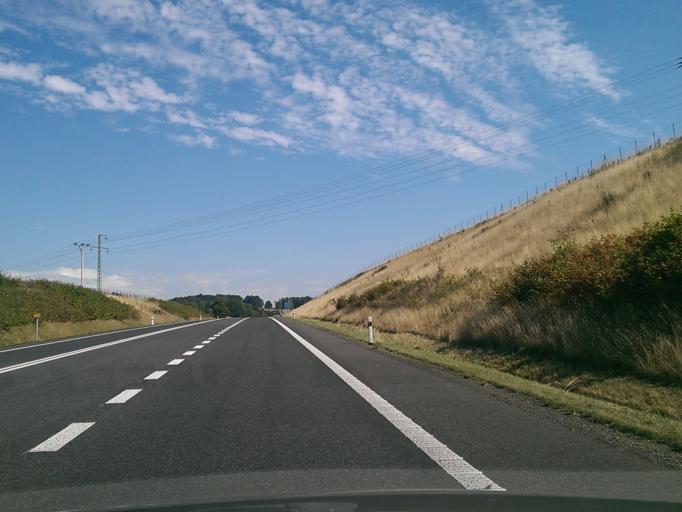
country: CZ
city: Chrastava
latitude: 50.8225
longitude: 14.9357
